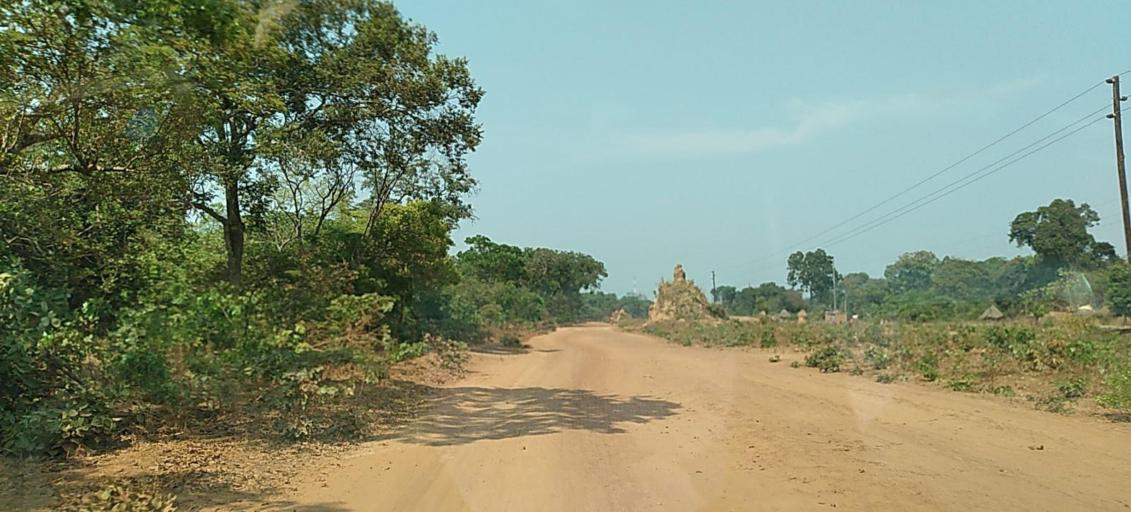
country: ZM
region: Copperbelt
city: Chingola
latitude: -13.0417
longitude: 27.4435
